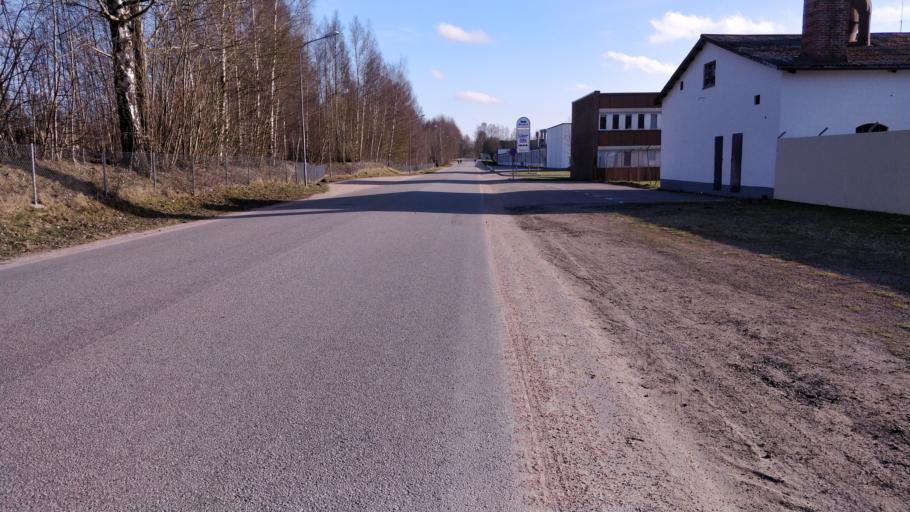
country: SE
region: Kronoberg
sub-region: Almhults Kommun
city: AElmhult
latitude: 56.5457
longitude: 14.1334
